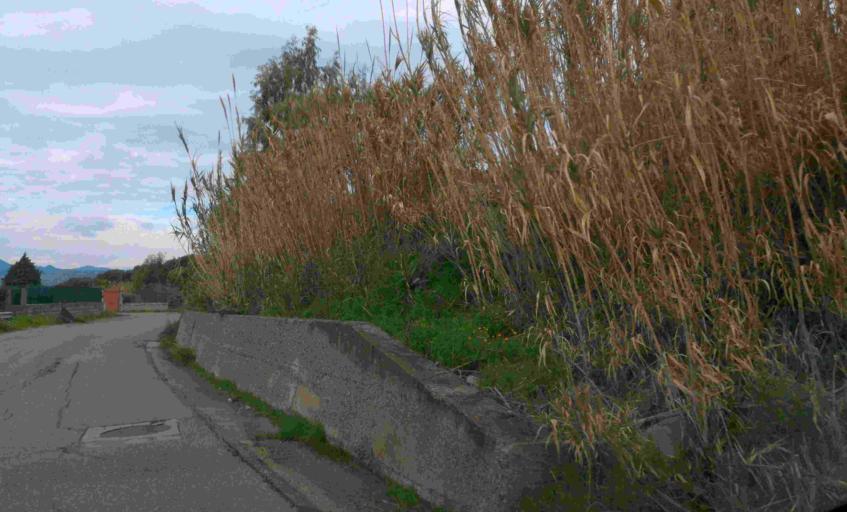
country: IT
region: Calabria
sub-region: Provincia di Catanzaro
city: Sellia Marina
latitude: 38.8880
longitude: 16.7095
